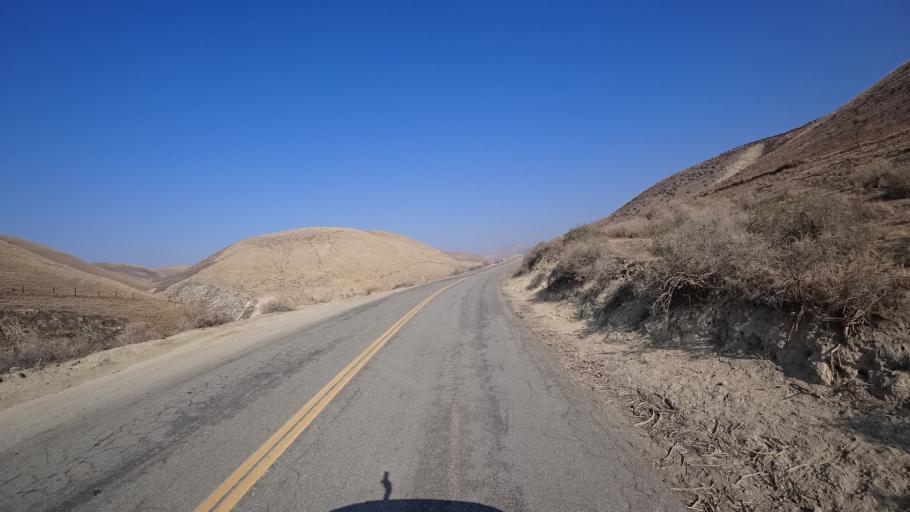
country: US
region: California
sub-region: Kern County
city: Oildale
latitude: 35.4480
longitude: -118.8283
